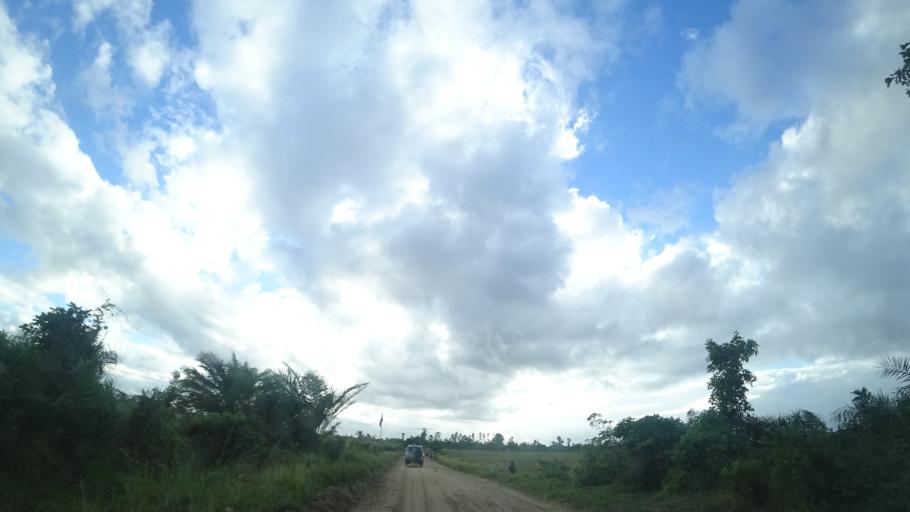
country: MZ
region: Sofala
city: Beira
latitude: -19.7206
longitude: 34.9996
